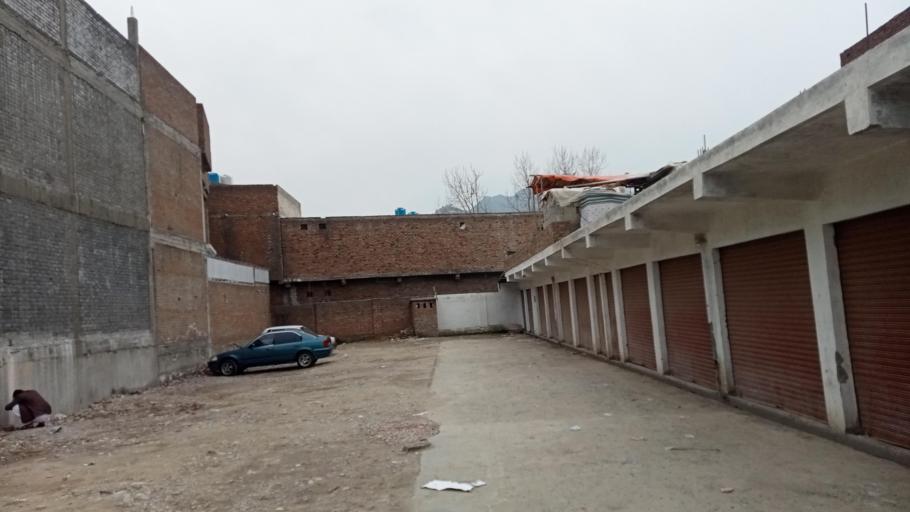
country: PK
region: Khyber Pakhtunkhwa
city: Mingora
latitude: 34.7771
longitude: 72.3488
